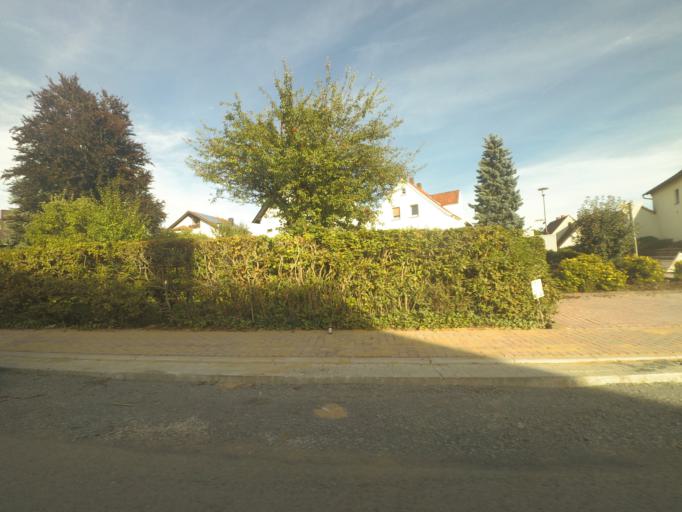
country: DE
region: Hesse
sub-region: Regierungsbezirk Kassel
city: Flieden
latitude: 50.4264
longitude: 9.5684
